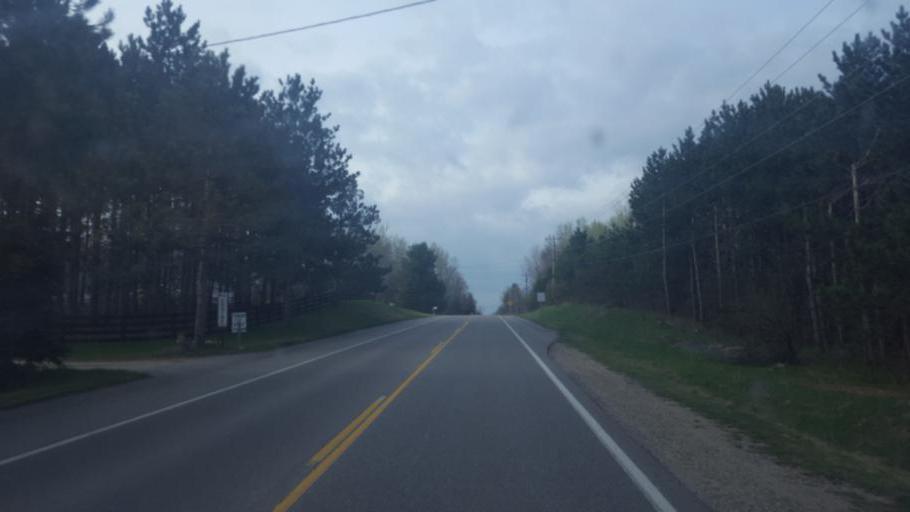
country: US
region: Michigan
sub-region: Isabella County
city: Lake Isabella
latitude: 43.5641
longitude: -84.9073
